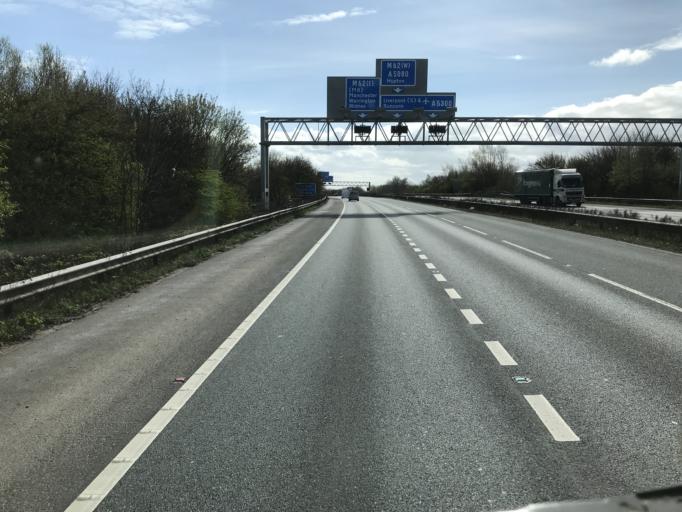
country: GB
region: England
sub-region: Knowsley
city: Prescot
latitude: 53.4082
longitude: -2.8137
